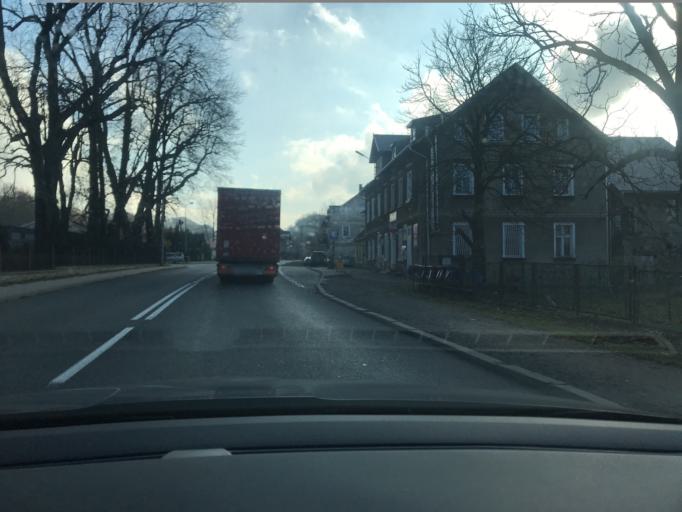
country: PL
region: Lower Silesian Voivodeship
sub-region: Powiat klodzki
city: Kudowa-Zdroj
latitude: 50.4224
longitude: 16.2582
